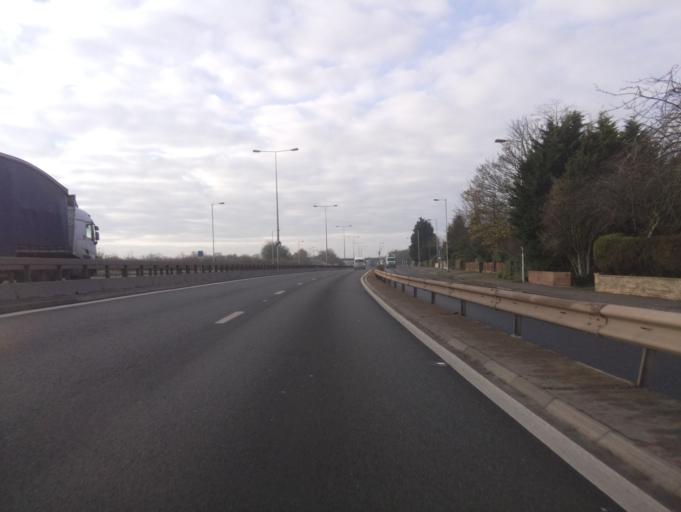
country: GB
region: England
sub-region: Staffordshire
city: Alrewas
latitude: 52.7298
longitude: -1.7421
